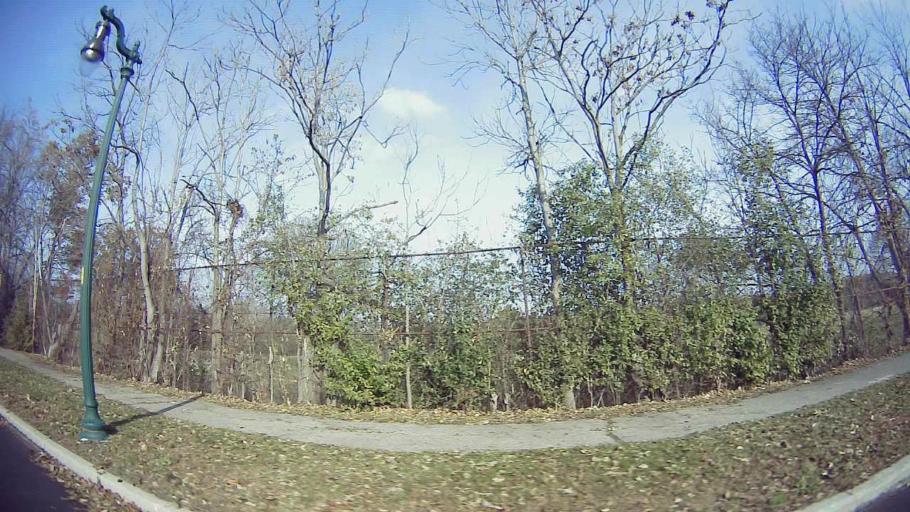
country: US
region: Michigan
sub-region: Wayne County
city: Highland Park
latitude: 42.4260
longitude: -83.1229
